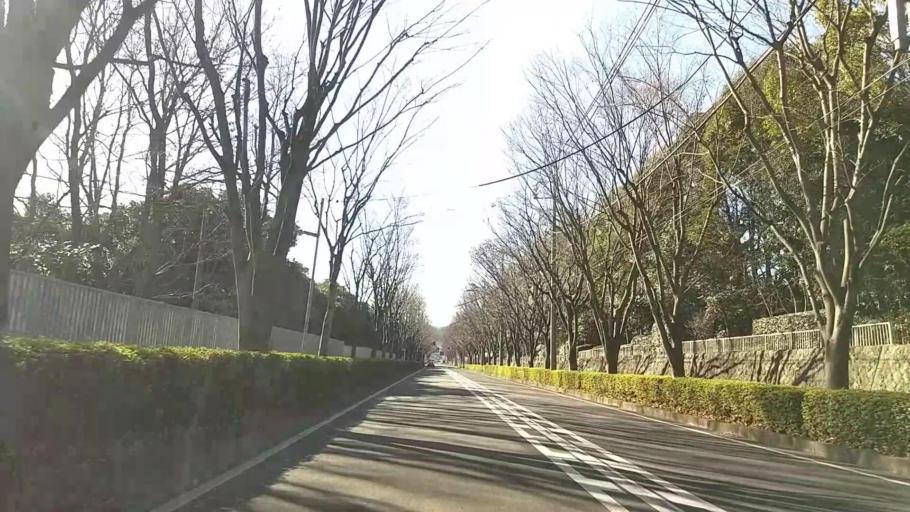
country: JP
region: Kanagawa
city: Hadano
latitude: 35.3857
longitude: 139.1890
